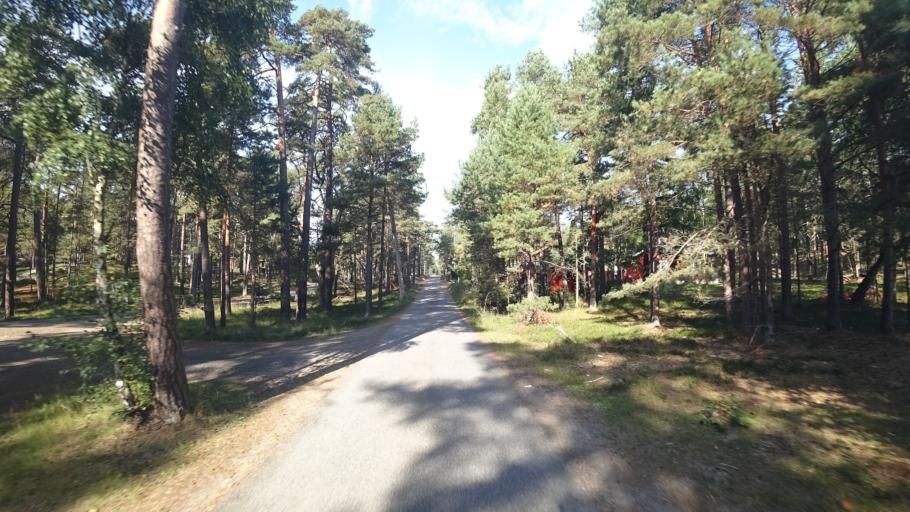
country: SE
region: Skane
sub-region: Kristianstads Kommun
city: Ahus
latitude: 55.9176
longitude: 14.3072
